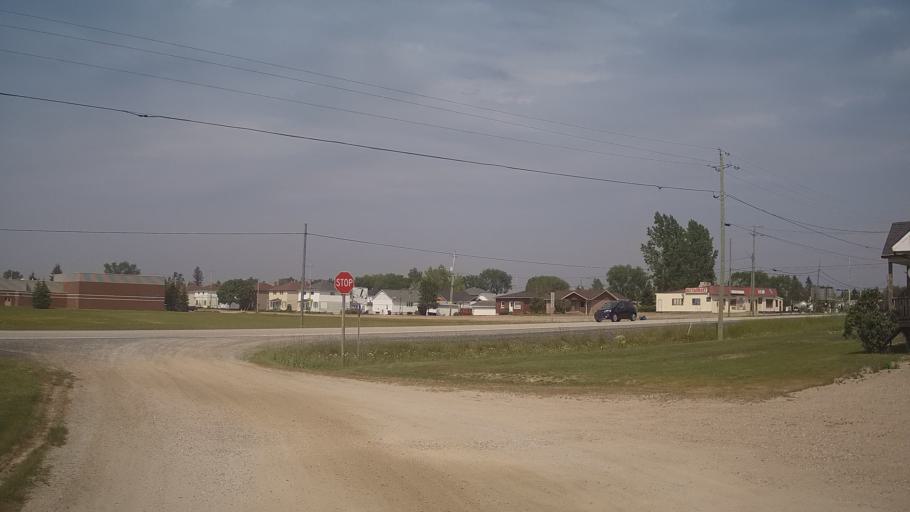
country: CA
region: Ontario
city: Kapuskasing
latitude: 49.2754
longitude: -81.6350
